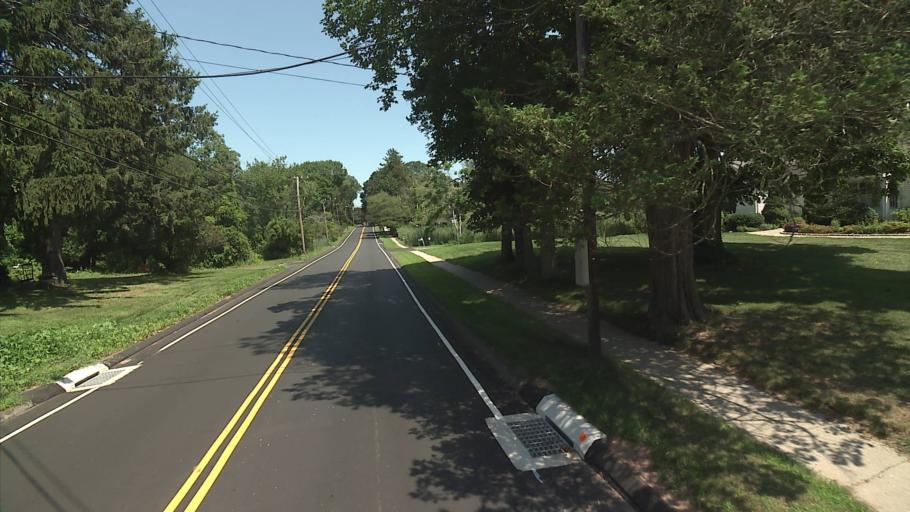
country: US
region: Connecticut
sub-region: Middlesex County
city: Old Saybrook Center
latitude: 41.2836
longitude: -72.3602
